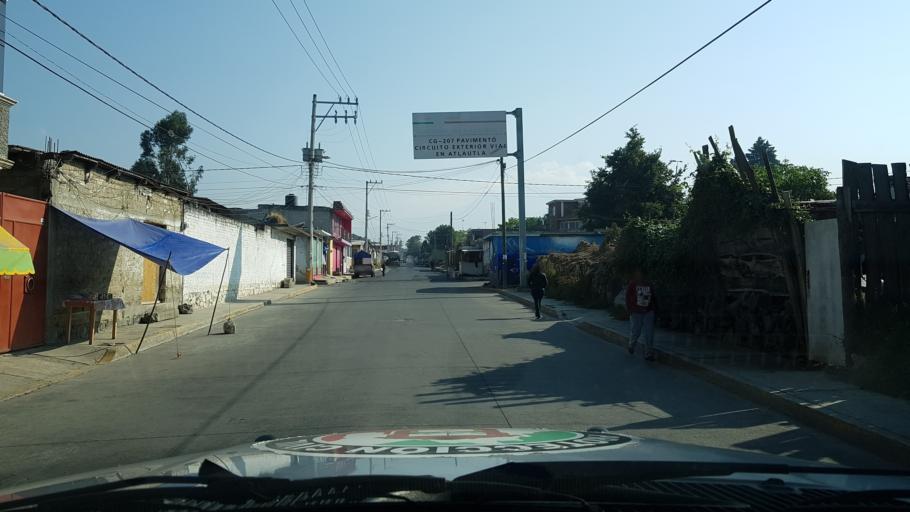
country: MX
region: Mexico
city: Atlautla
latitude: 19.0327
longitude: -98.7784
